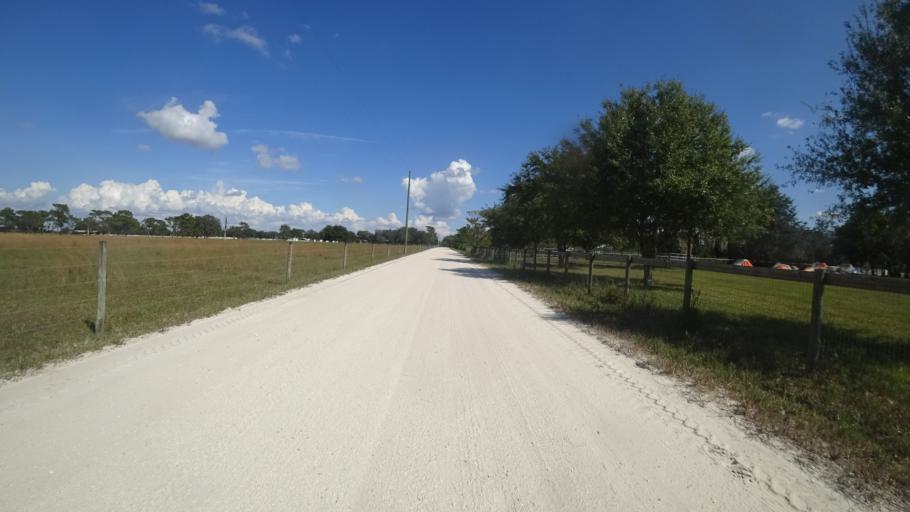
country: US
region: Florida
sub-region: Sarasota County
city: The Meadows
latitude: 27.4525
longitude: -82.2936
